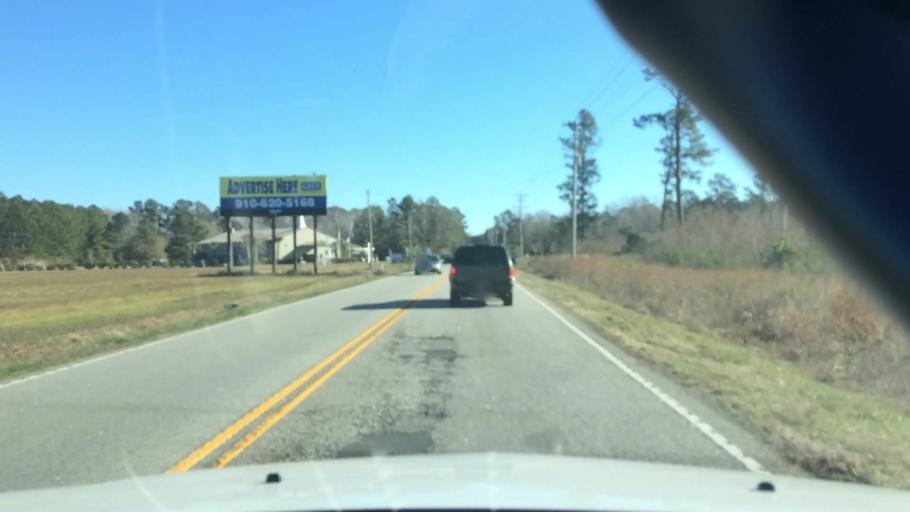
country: US
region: South Carolina
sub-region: Horry County
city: Little River
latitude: 33.9057
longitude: -78.6602
